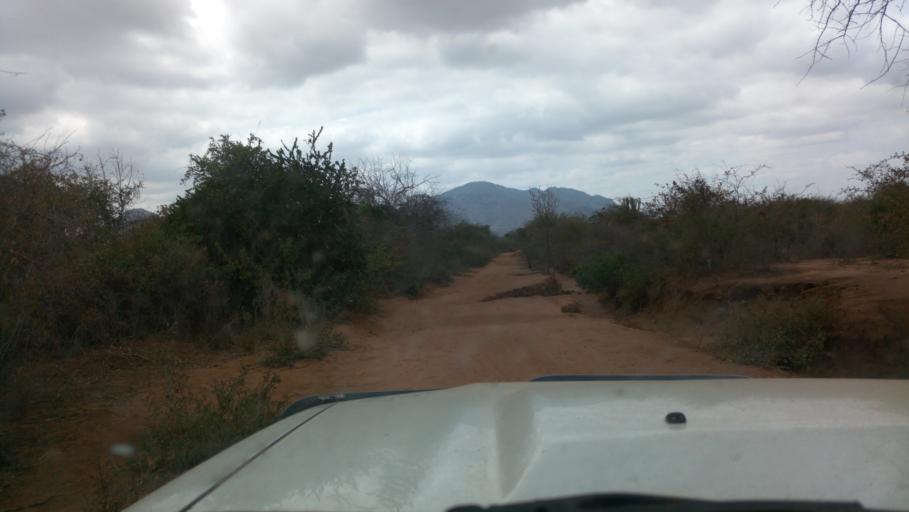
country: KE
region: Kitui
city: Kitui
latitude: -1.8506
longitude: 38.3520
